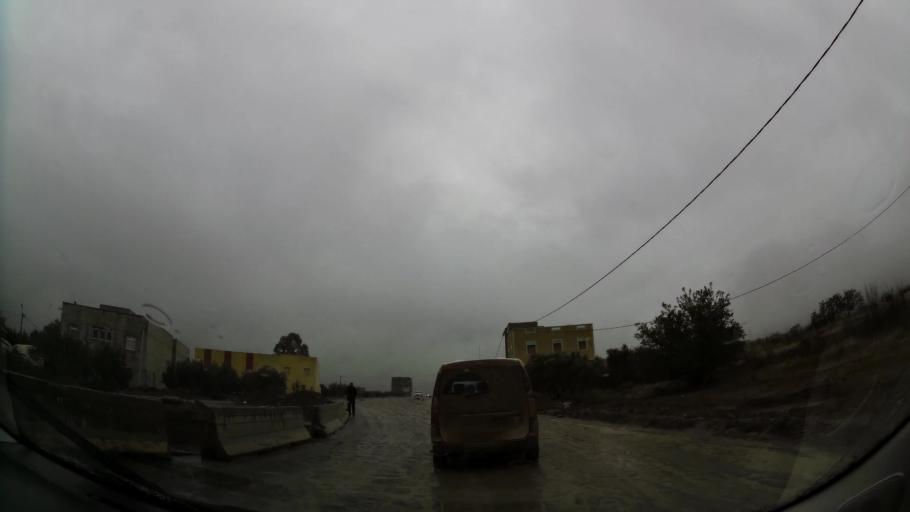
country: MA
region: Oriental
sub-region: Nador
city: Midar
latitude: 34.8720
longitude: -3.7259
